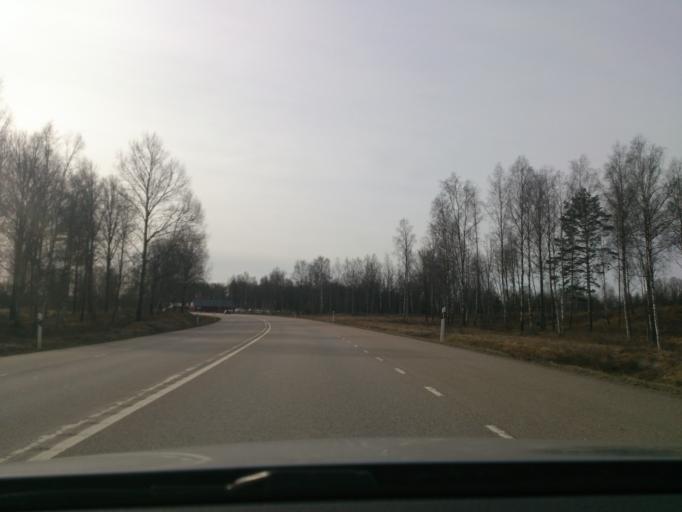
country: SE
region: Kronoberg
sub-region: Alvesta Kommun
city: Alvesta
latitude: 56.9144
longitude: 14.5532
